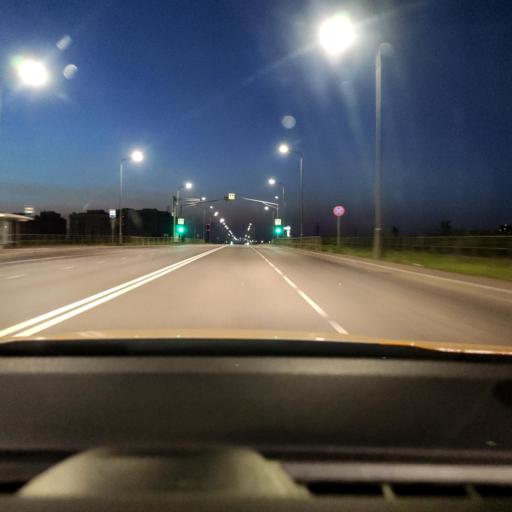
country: RU
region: Moskovskaya
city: Shcherbinka
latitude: 55.4935
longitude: 37.5221
